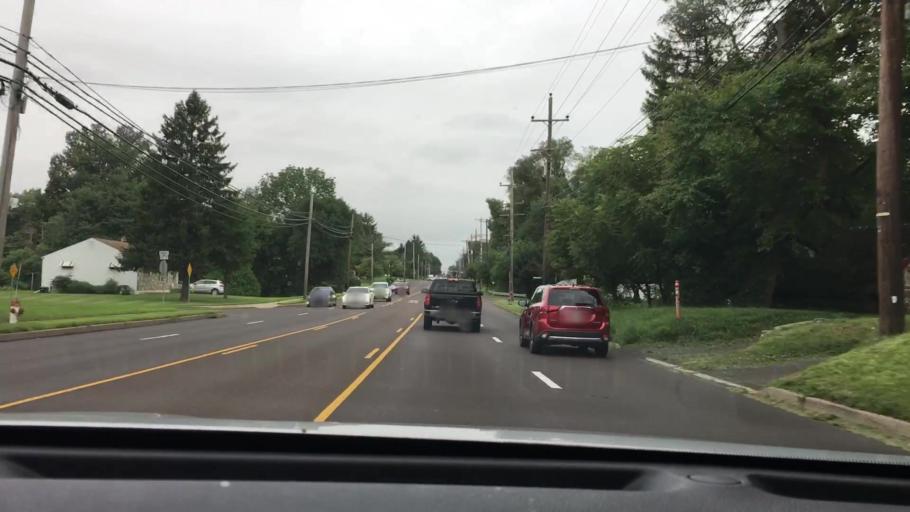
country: US
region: Pennsylvania
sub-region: Montgomery County
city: Hatboro
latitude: 40.1943
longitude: -75.1102
